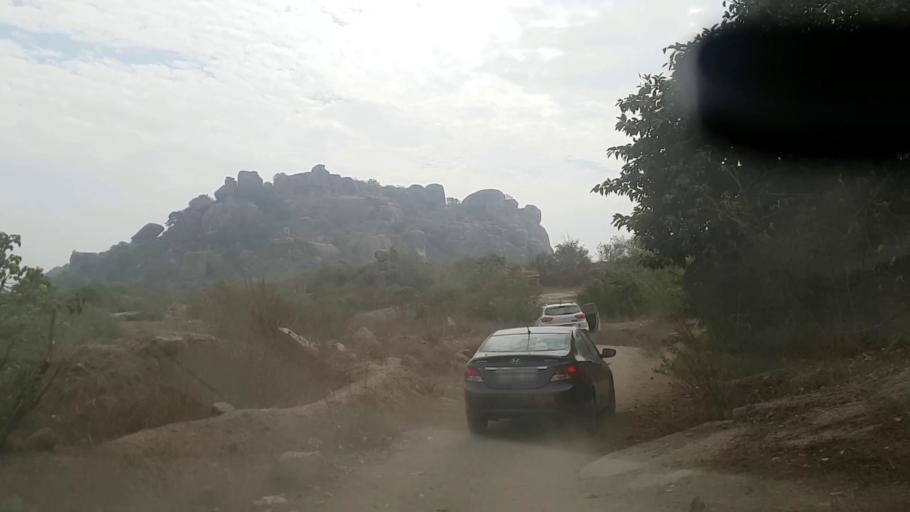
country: IN
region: Telangana
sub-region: Rangareddi
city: Ghatkesar
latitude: 17.1798
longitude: 78.8006
